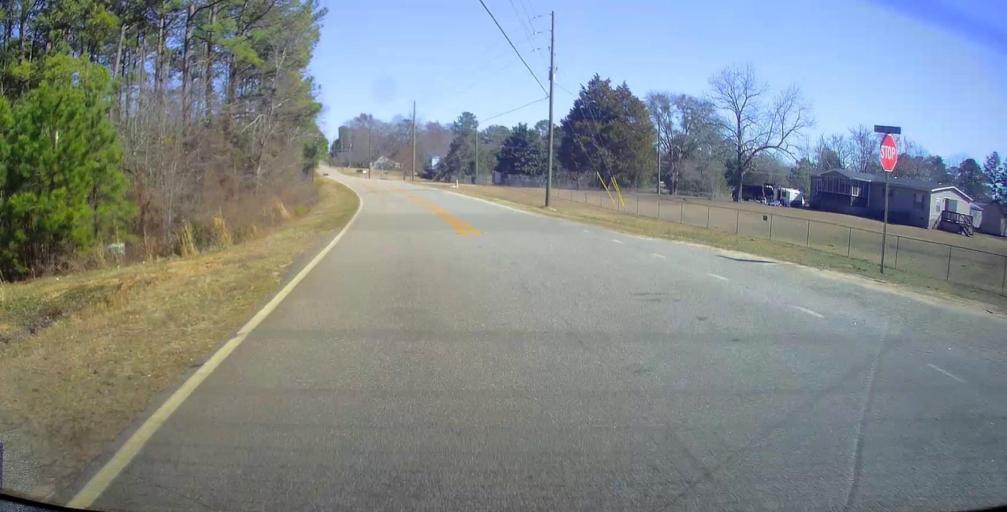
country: US
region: Georgia
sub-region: Peach County
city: Byron
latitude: 32.6193
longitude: -83.7798
